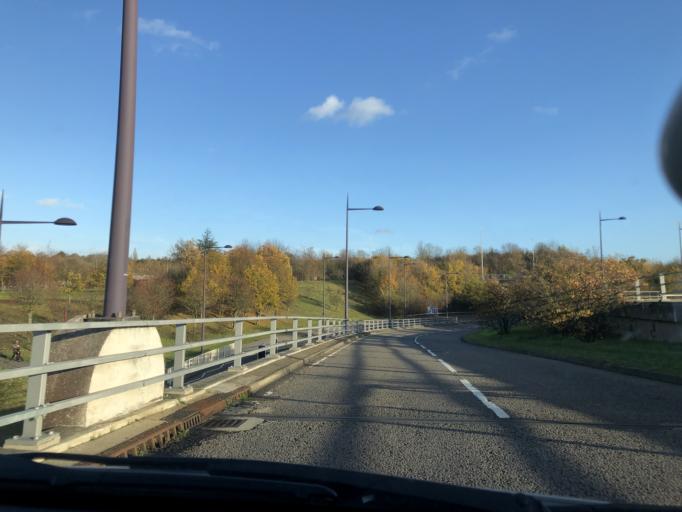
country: GB
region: England
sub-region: Kent
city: Greenhithe
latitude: 51.4414
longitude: 0.2777
